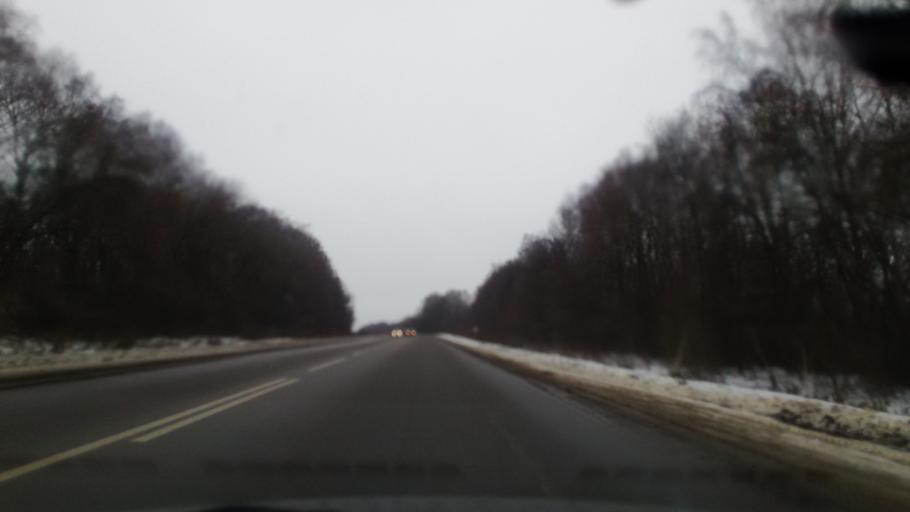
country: RU
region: Tula
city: Bolokhovo
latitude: 54.0469
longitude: 37.8509
